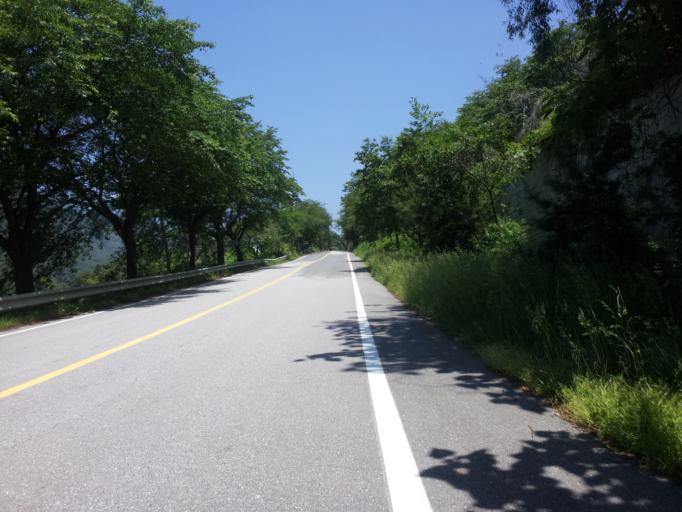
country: KR
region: Chungcheongbuk-do
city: Okcheon
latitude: 36.3679
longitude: 127.6108
